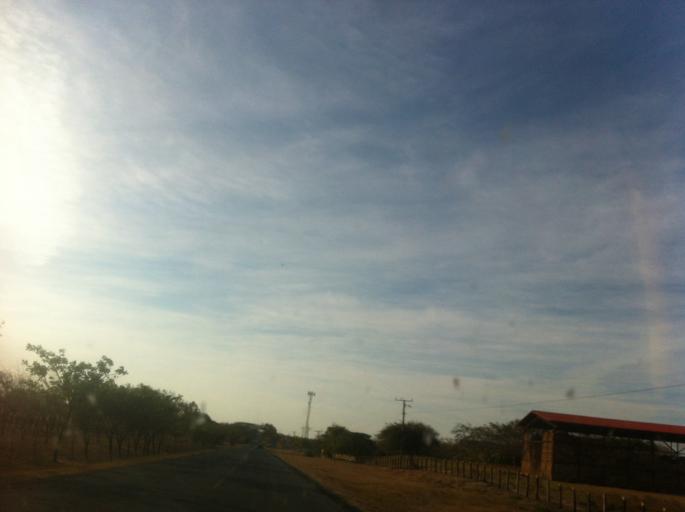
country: NI
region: Rivas
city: Rivas
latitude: 11.3465
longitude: -85.7366
